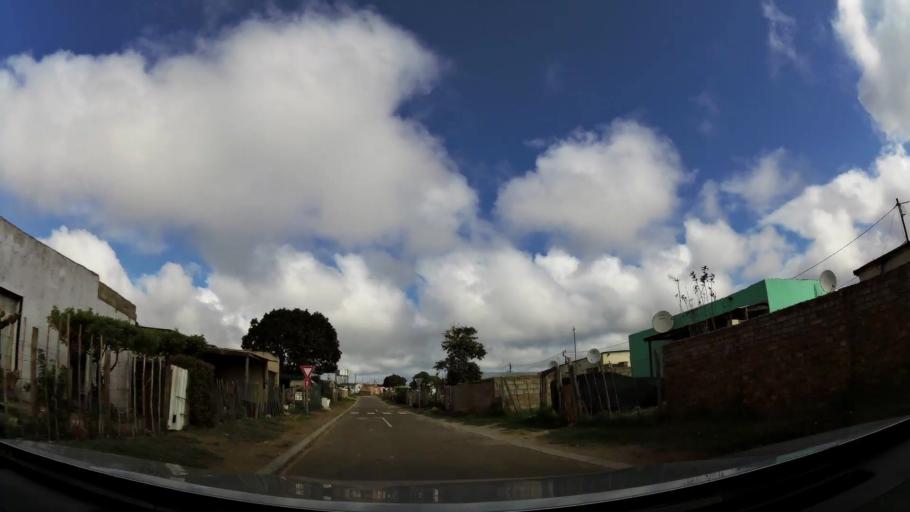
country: ZA
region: Western Cape
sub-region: Eden District Municipality
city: Plettenberg Bay
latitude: -34.0508
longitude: 23.3227
